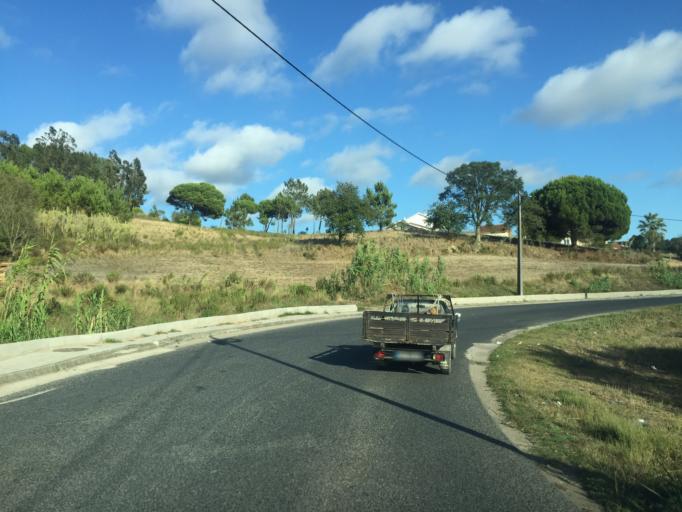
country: PT
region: Lisbon
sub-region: Torres Vedras
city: A dos Cunhados
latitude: 39.1491
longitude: -9.2884
